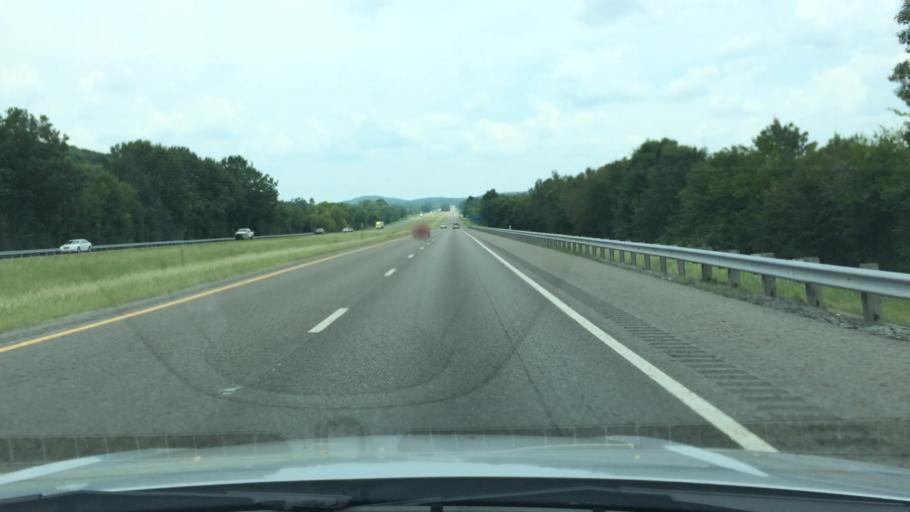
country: US
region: Tennessee
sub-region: Marshall County
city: Cornersville
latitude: 35.4249
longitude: -86.8784
